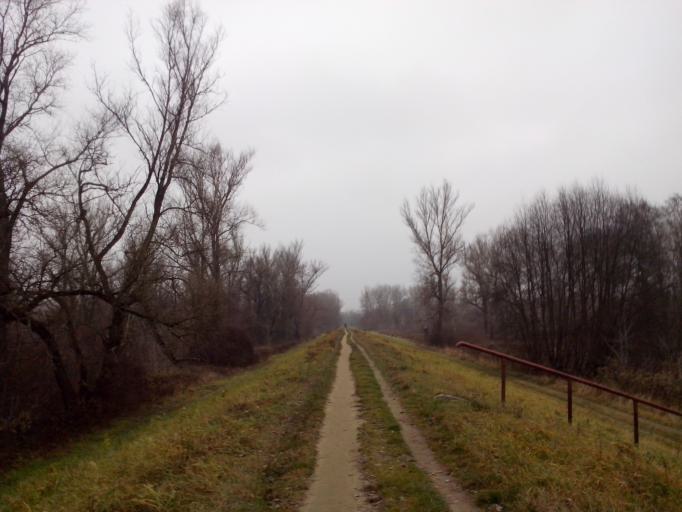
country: PL
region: Masovian Voivodeship
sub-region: Powiat legionowski
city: Jablonna
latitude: 52.3560
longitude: 20.9203
